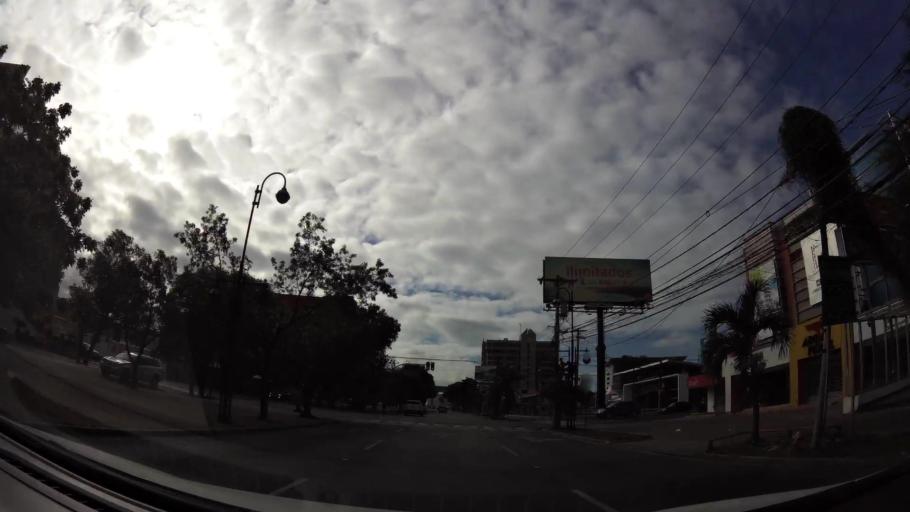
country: DO
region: Nacional
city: La Julia
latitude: 18.4655
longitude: -69.9378
